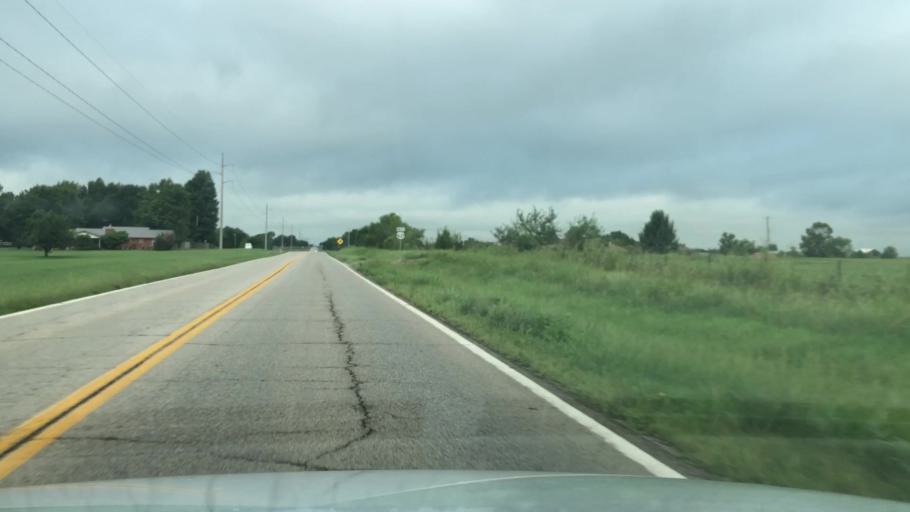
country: US
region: Oklahoma
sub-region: Nowata County
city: Nowata
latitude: 36.7136
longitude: -95.6768
